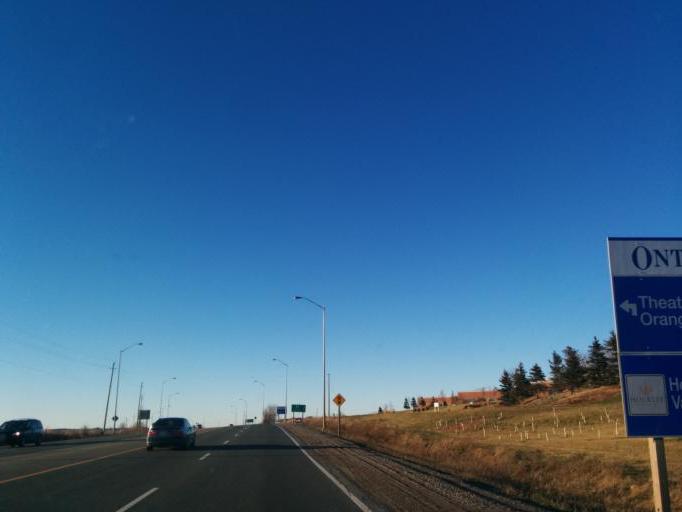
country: CA
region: Ontario
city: Orangeville
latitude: 43.9171
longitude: -80.0733
